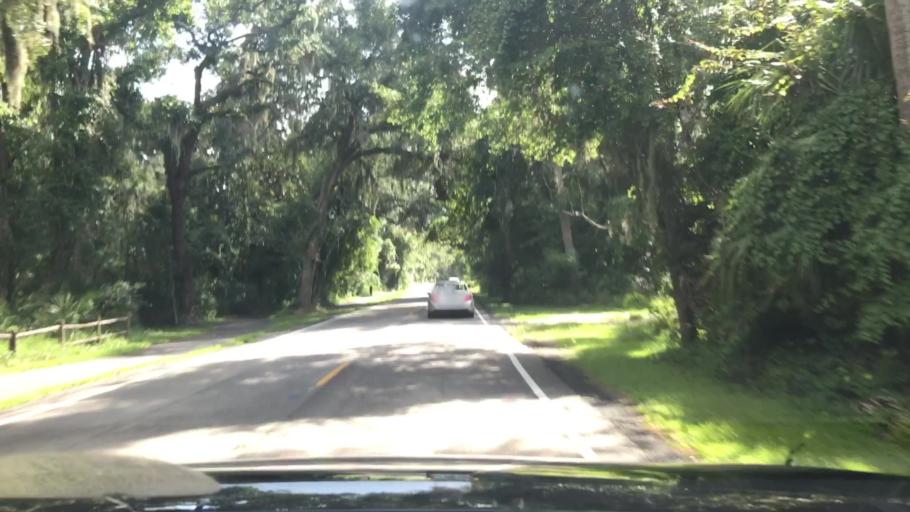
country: US
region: South Carolina
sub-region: Beaufort County
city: Hilton Head Island
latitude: 32.1400
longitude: -80.7675
